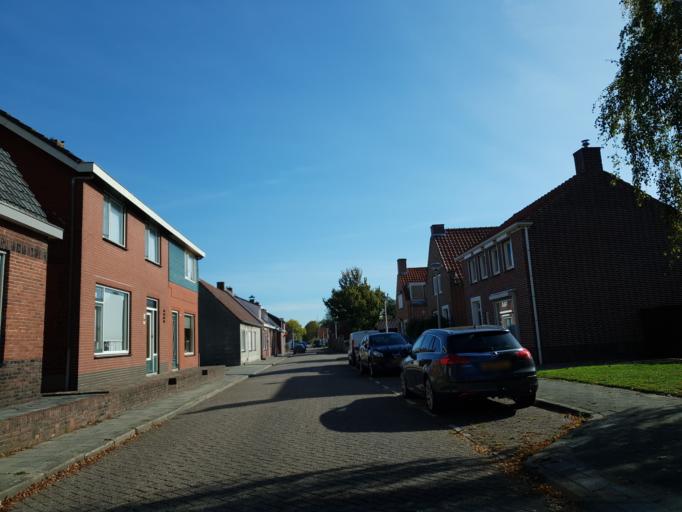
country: NL
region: North Brabant
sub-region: Gemeente Woensdrecht
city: Woensdrecht
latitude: 51.3948
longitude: 4.3333
